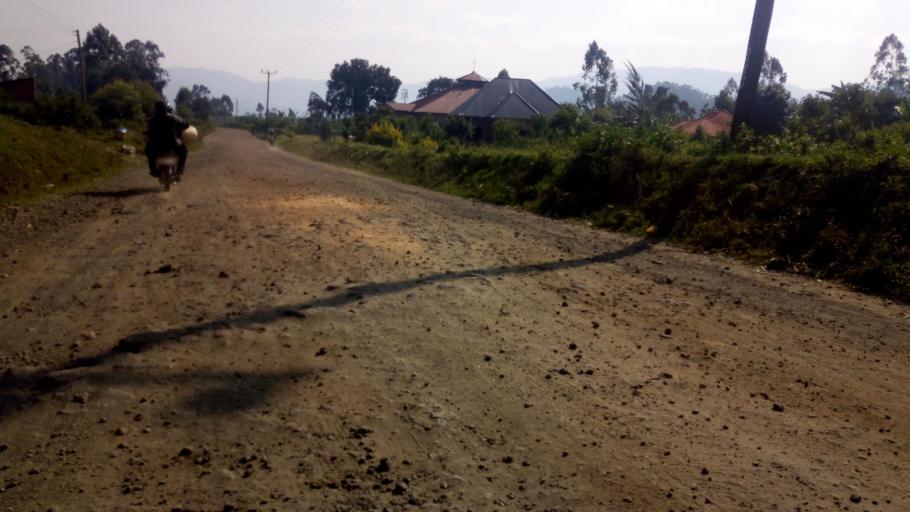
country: UG
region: Western Region
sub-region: Kisoro District
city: Kisoro
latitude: -1.2535
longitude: 29.7136
